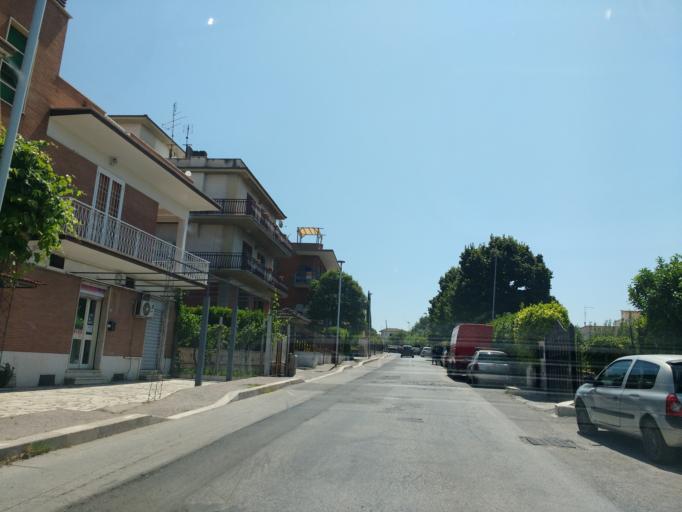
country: IT
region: Latium
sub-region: Citta metropolitana di Roma Capitale
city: Villa Adriana
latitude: 41.9491
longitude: 12.7723
